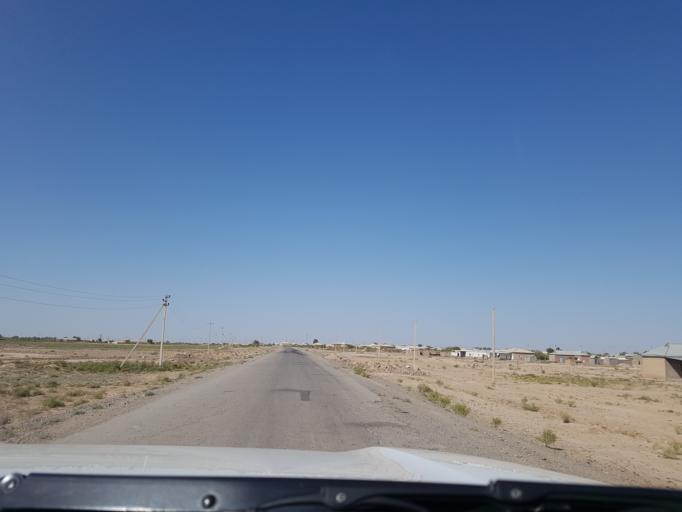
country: IR
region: Razavi Khorasan
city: Sarakhs
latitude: 36.5096
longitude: 61.2533
